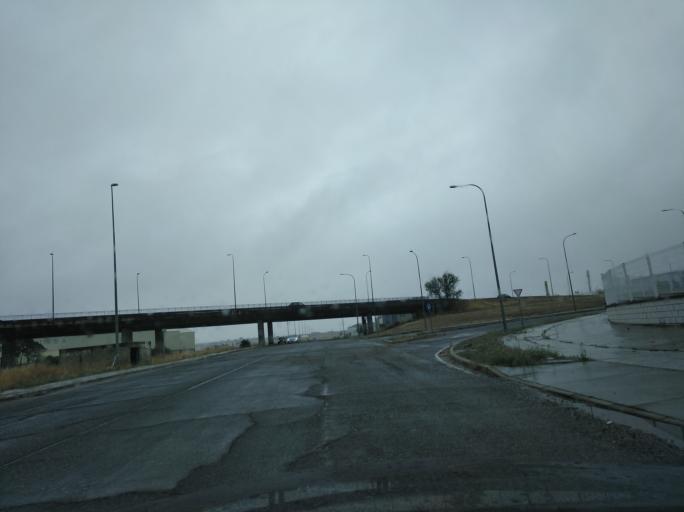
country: ES
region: Extremadura
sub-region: Provincia de Badajoz
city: Badajoz
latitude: 38.8965
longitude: -6.9905
